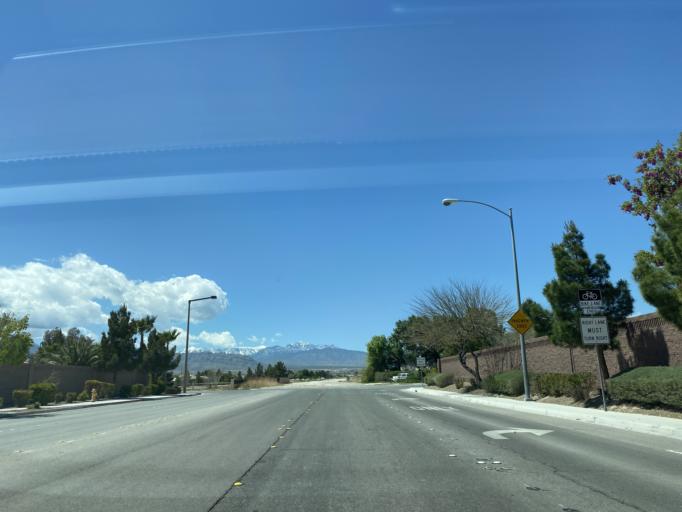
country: US
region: Nevada
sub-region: Clark County
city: North Las Vegas
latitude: 36.3128
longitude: -115.2303
